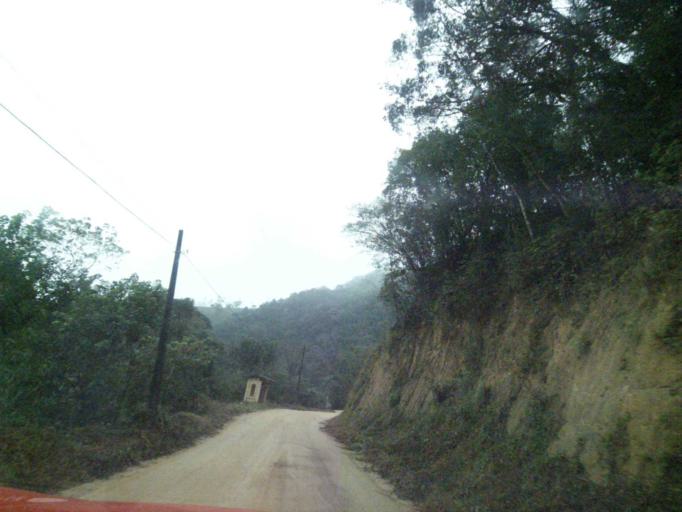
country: BR
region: Santa Catarina
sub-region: Anitapolis
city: Anitapolis
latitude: -27.9242
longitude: -49.1309
